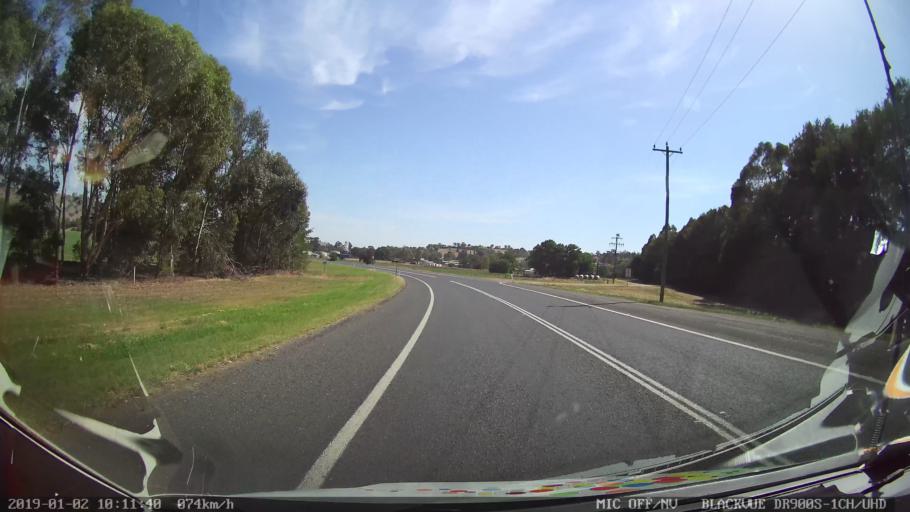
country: AU
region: New South Wales
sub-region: Gundagai
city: Gundagai
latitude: -35.0909
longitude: 148.0944
